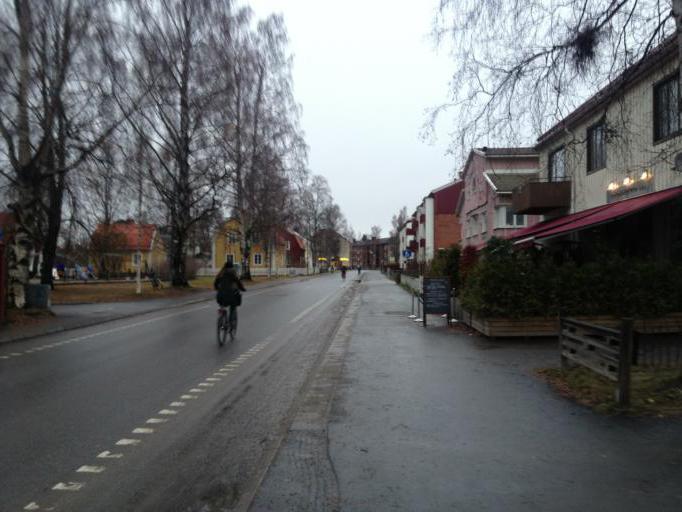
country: SE
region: Vaesterbotten
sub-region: Umea Kommun
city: Umea
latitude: 63.8209
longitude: 20.2874
